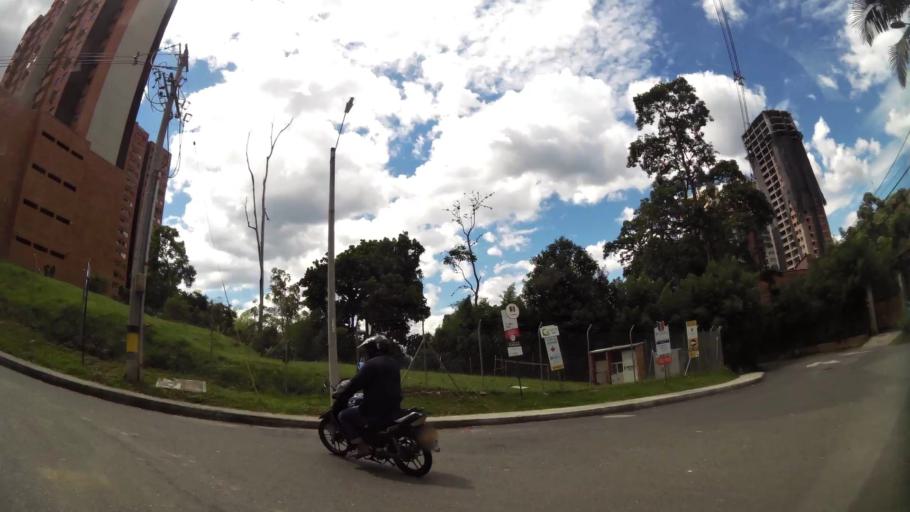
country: CO
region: Antioquia
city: Sabaneta
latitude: 6.1443
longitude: -75.6168
